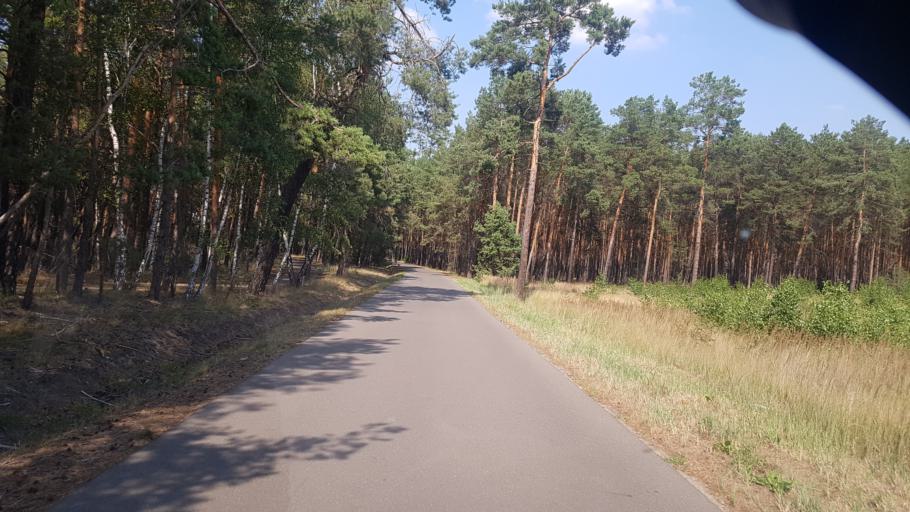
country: DE
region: Brandenburg
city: Spremberg
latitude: 51.6217
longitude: 14.4008
